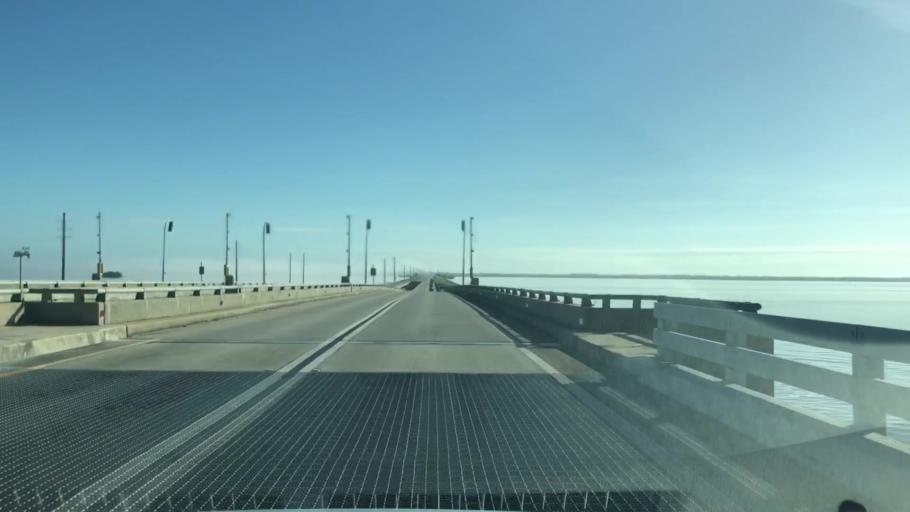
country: US
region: Florida
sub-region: Brevard County
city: Port Saint John
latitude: 28.5273
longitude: -80.7654
